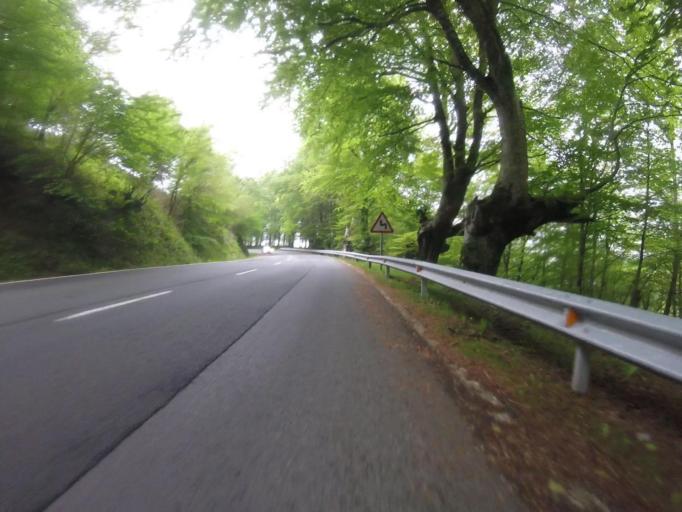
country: ES
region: Navarre
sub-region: Provincia de Navarra
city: Zugarramurdi
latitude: 43.2435
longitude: -1.4808
